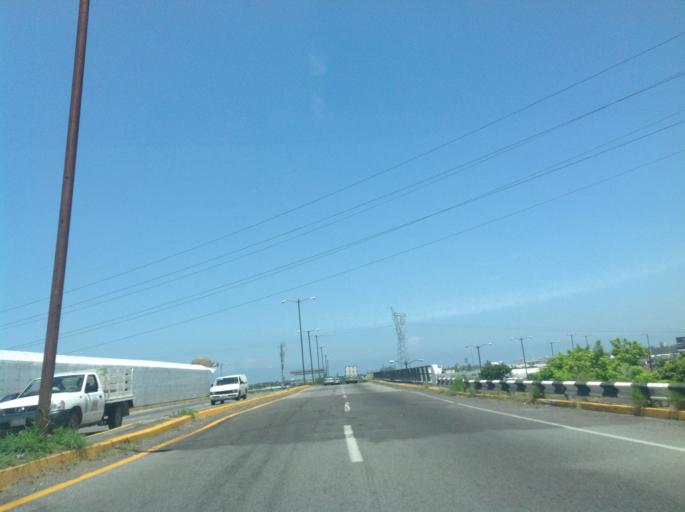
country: MX
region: Veracruz
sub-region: Veracruz
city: Hacienda Sotavento
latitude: 19.1395
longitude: -96.1496
